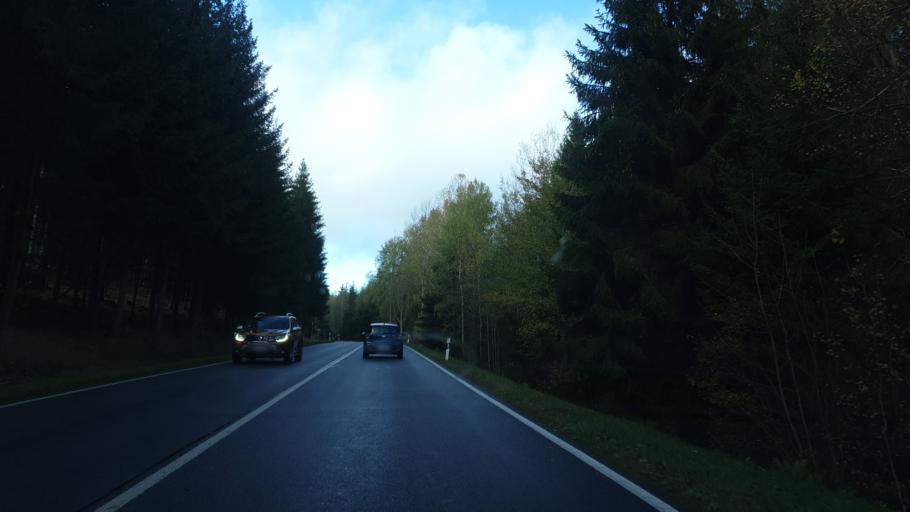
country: DE
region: Saxony
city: Eibenstock
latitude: 50.5092
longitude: 12.6042
